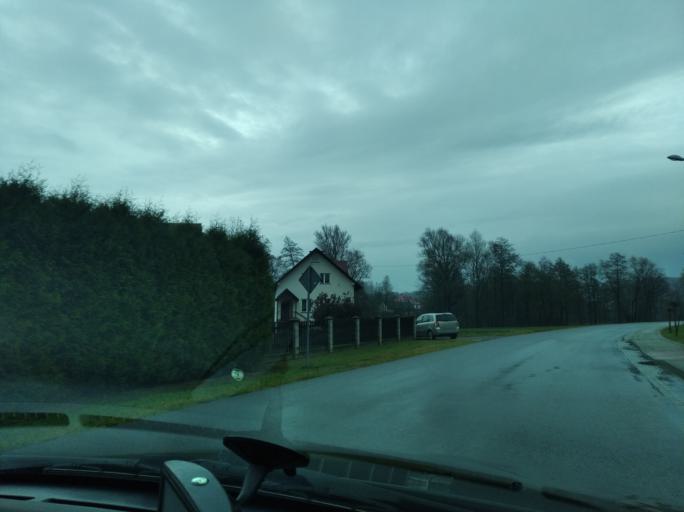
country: PL
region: Subcarpathian Voivodeship
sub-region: Powiat rzeszowski
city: Lubenia
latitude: 49.9230
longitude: 21.9504
